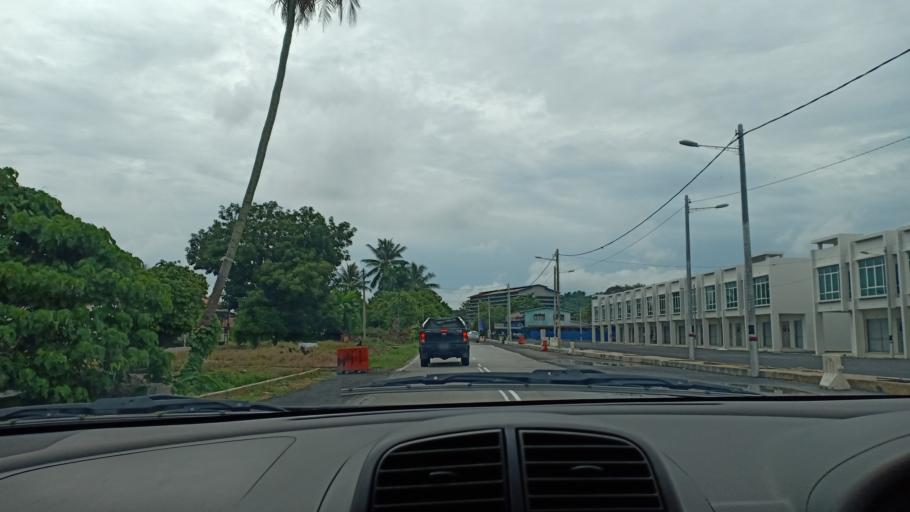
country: MY
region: Penang
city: Bukit Mertajam
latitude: 5.4080
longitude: 100.4791
